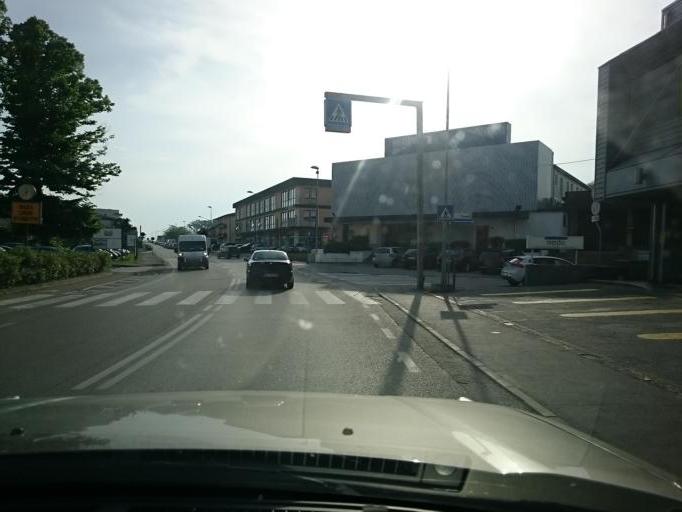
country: IT
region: Veneto
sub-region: Provincia di Padova
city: Oltre Brenta
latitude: 45.4110
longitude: 12.0023
